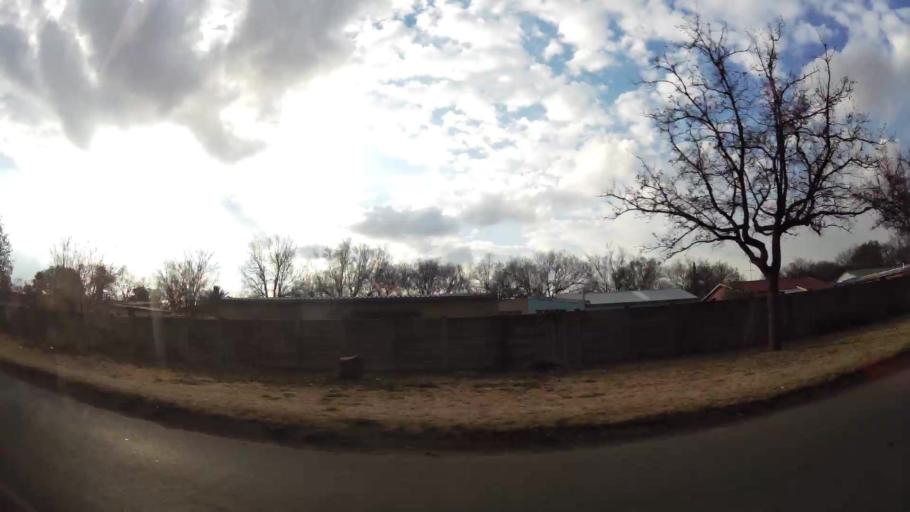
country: ZA
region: Orange Free State
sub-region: Fezile Dabi District Municipality
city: Sasolburg
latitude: -26.8269
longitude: 27.8213
